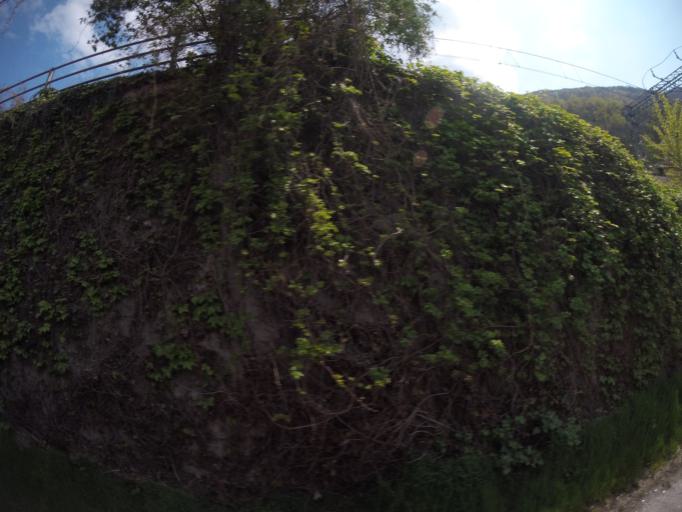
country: IT
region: Piedmont
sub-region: Provincia Verbano-Cusio-Ossola
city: Omegna
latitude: 45.8669
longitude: 8.4139
